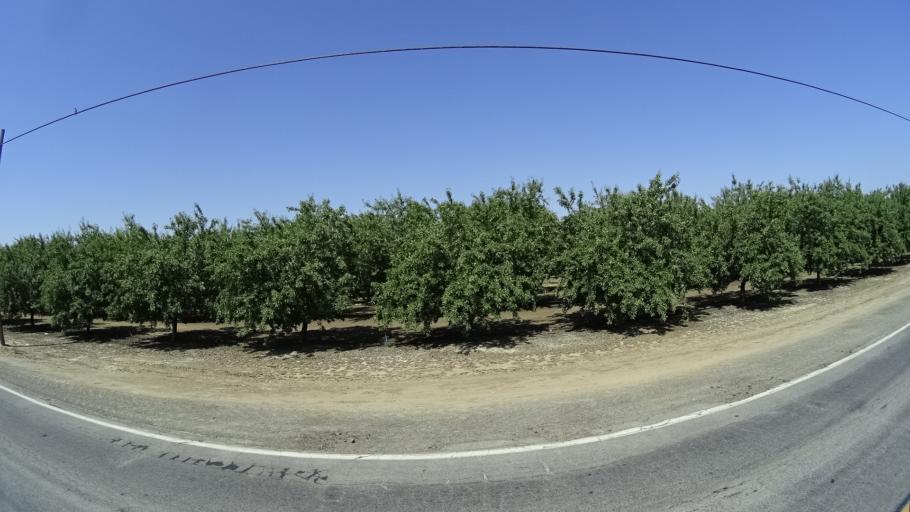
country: US
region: California
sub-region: Kings County
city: Home Garden
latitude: 36.3121
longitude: -119.6190
